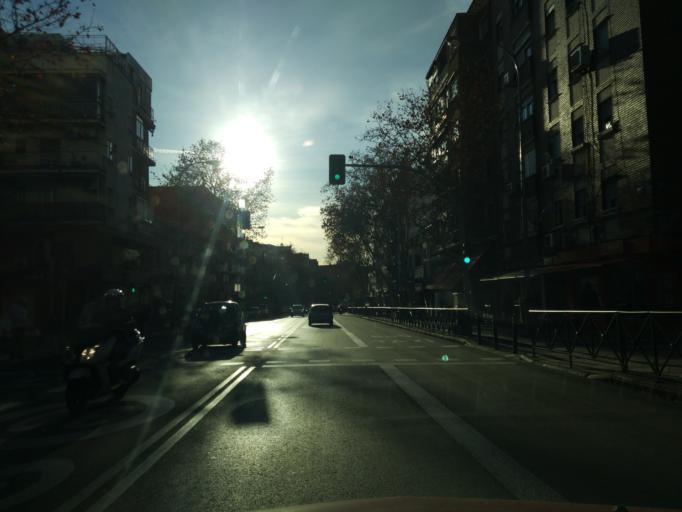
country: ES
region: Madrid
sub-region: Provincia de Madrid
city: Moratalaz
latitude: 40.4341
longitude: -3.6460
